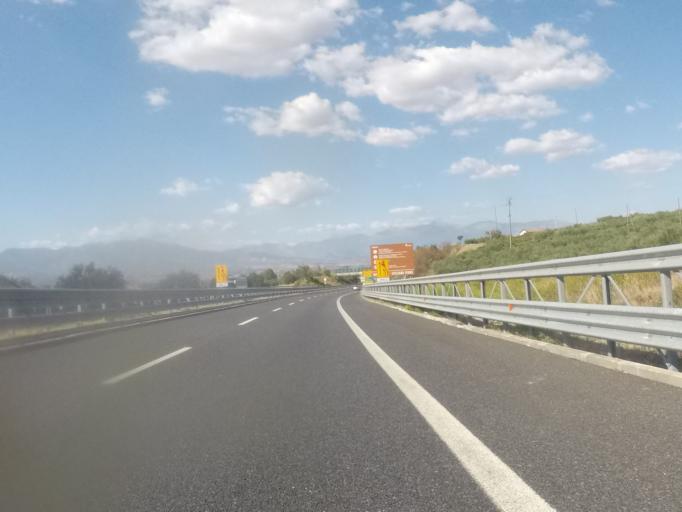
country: IT
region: Calabria
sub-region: Provincia di Cosenza
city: Tarsia
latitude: 39.6140
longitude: 16.2305
